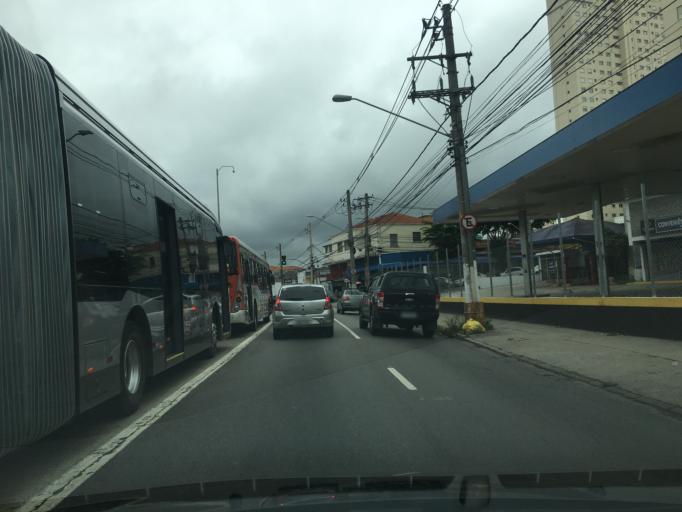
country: BR
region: Sao Paulo
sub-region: Taboao Da Serra
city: Taboao da Serra
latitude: -23.5849
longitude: -46.7190
